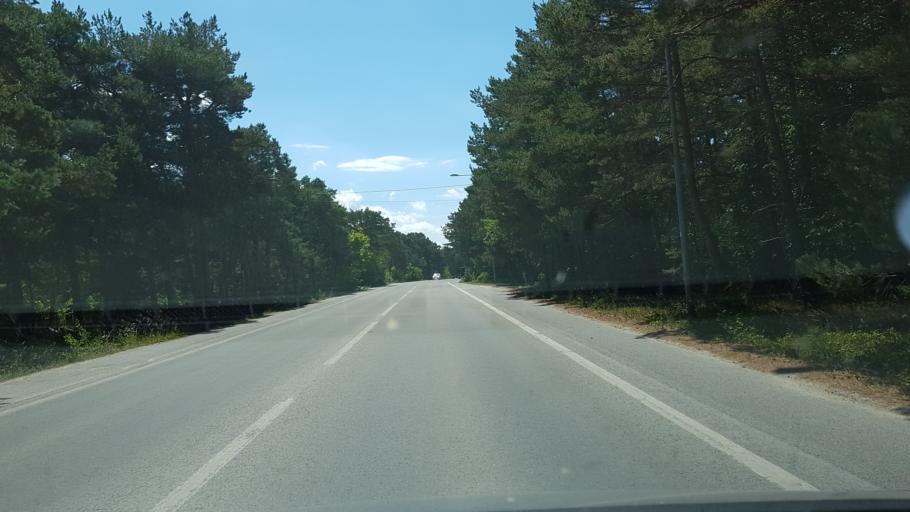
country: SE
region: Gotland
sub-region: Gotland
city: Visby
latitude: 57.6658
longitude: 18.3341
